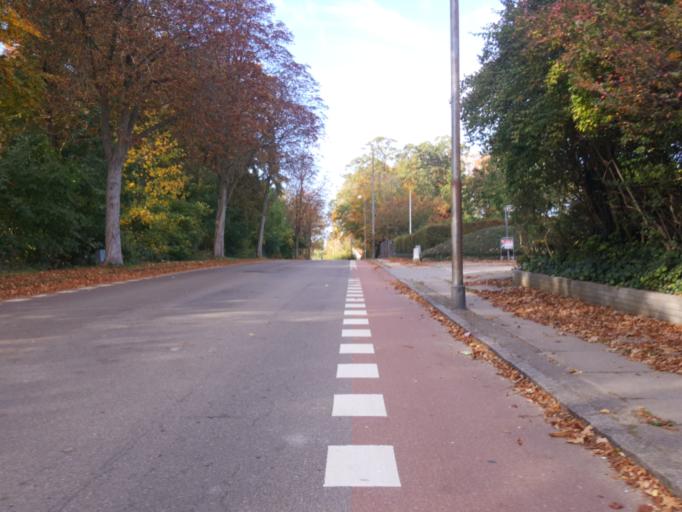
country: DK
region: Zealand
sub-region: Kalundborg Kommune
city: Kalundborg
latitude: 55.6896
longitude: 11.0752
